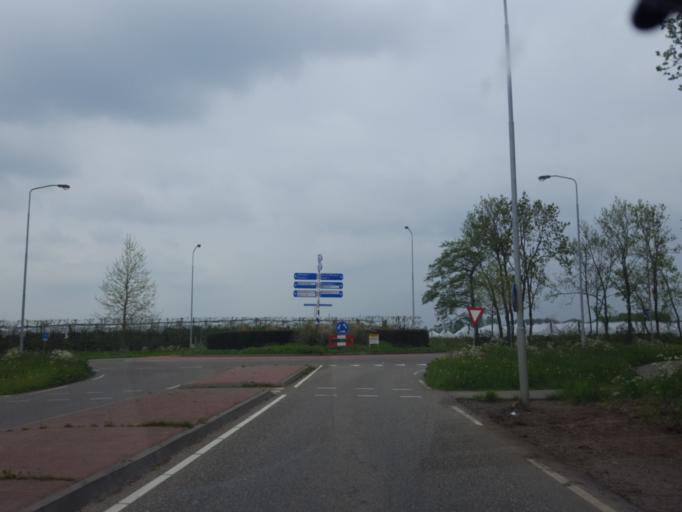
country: NL
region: Gelderland
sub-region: Gemeente Wijchen
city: Bergharen
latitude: 51.8818
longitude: 5.6617
